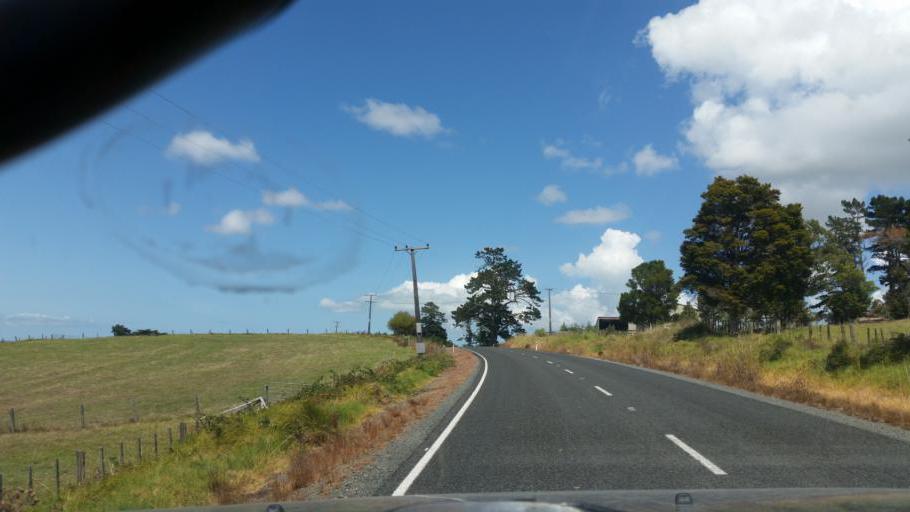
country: NZ
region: Northland
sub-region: Whangarei
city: Ruakaka
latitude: -36.1259
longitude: 174.2310
